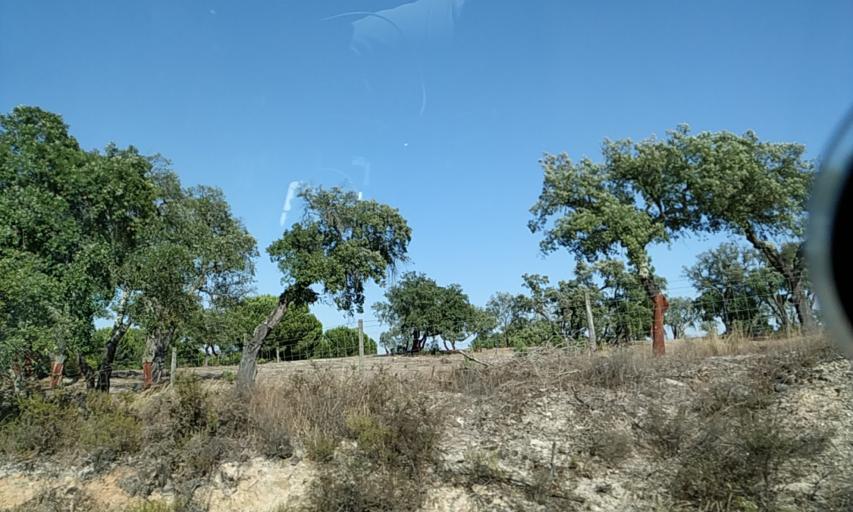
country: PT
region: Santarem
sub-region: Coruche
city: Coruche
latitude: 38.8585
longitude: -8.5450
